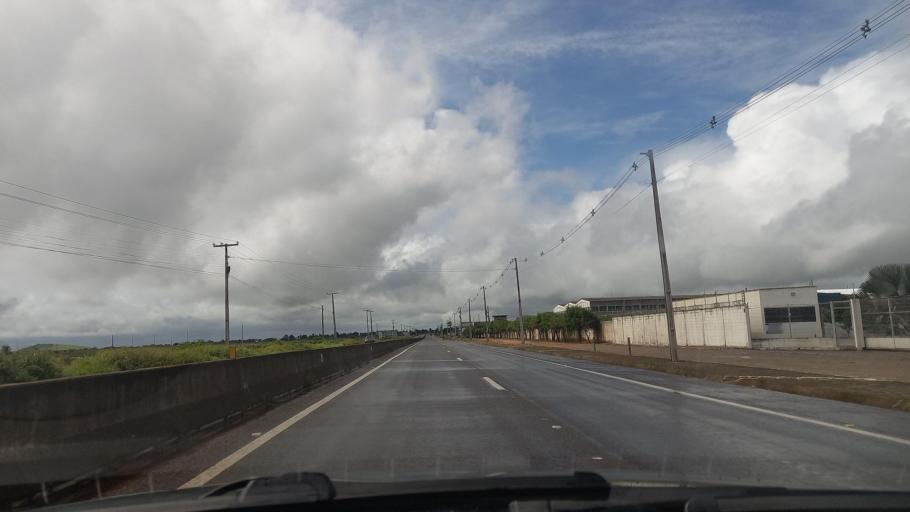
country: BR
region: Alagoas
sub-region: Limoeiro De Anadia
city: Limoeiro de Anadia
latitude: -9.7605
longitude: -36.5450
